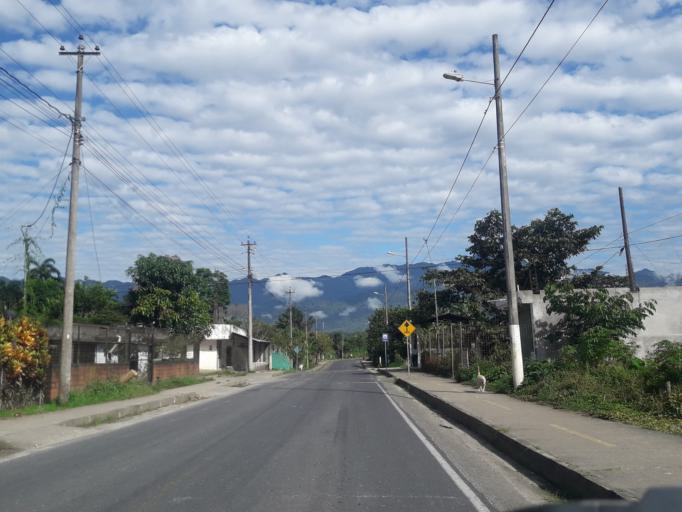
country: EC
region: Napo
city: Tena
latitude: -0.9847
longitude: -77.8386
